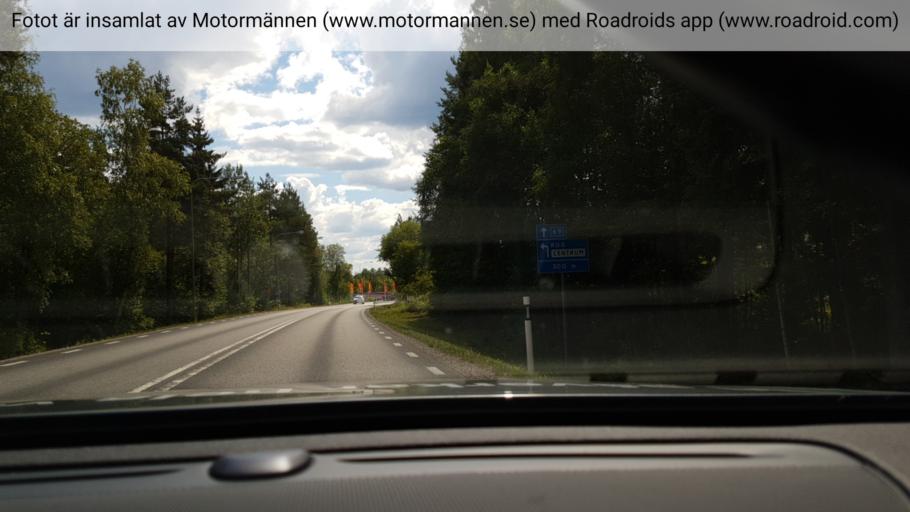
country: SE
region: Dalarna
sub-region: Faluns Kommun
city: Bjursas
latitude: 60.7361
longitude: 15.4355
